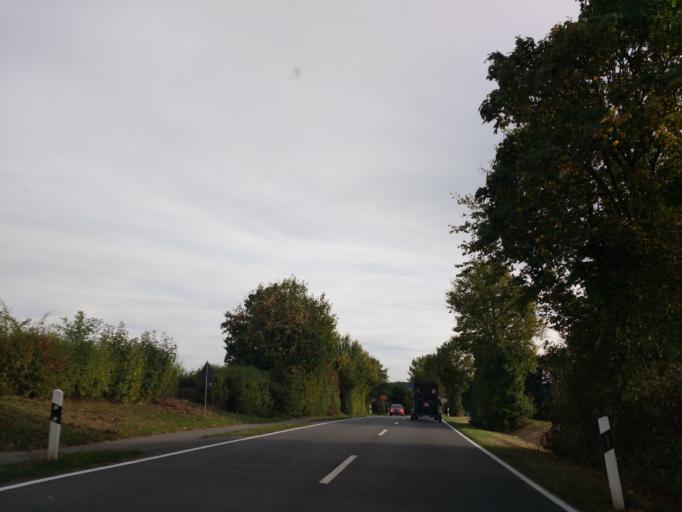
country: DE
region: North Rhine-Westphalia
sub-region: Regierungsbezirk Detmold
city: Bad Meinberg
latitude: 51.9372
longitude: 9.0241
